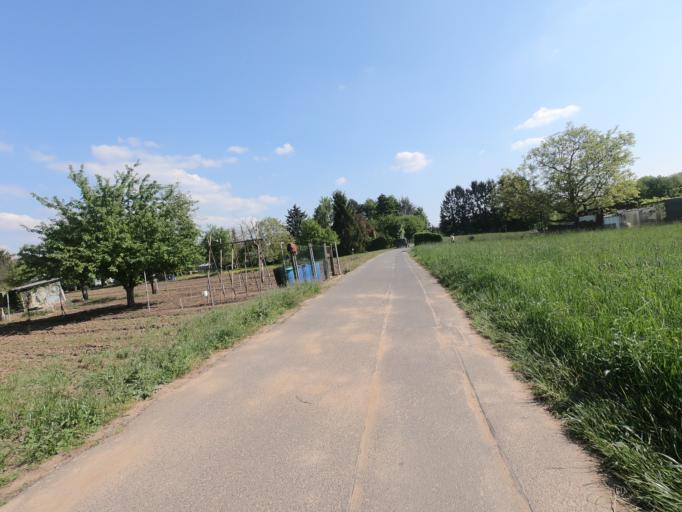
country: DE
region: Hesse
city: Kelsterbach
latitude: 50.0737
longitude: 8.5263
